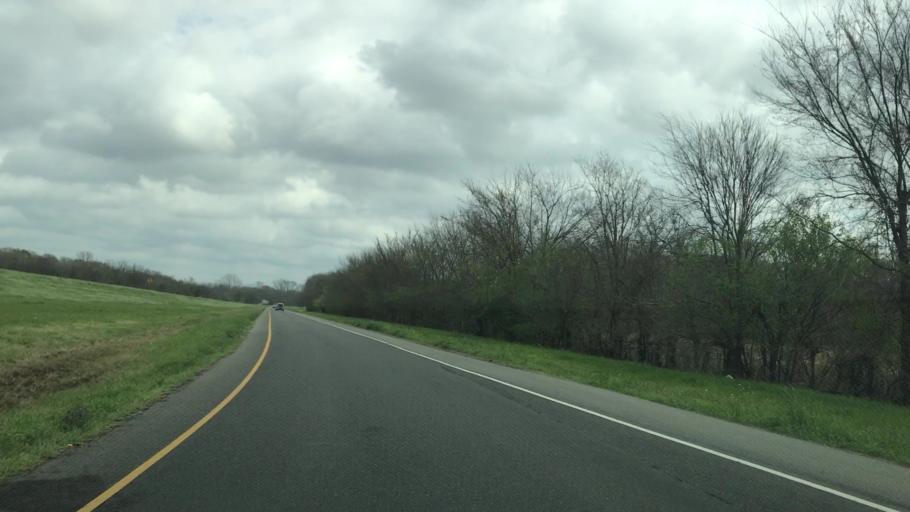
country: US
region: Louisiana
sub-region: Rapides Parish
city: Boyce
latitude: 31.3785
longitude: -92.6687
